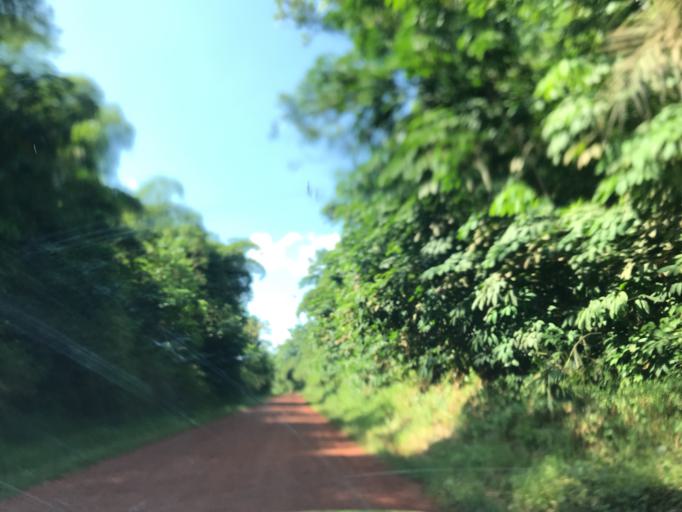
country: CD
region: Eastern Province
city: Kisangani
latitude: 1.2628
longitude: 25.2792
